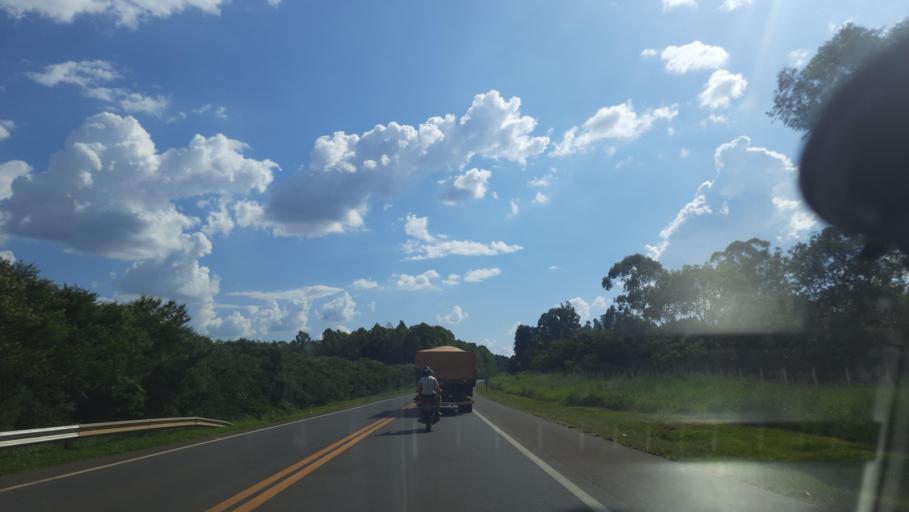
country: BR
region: Sao Paulo
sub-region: Casa Branca
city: Casa Branca
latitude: -21.7552
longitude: -47.0016
